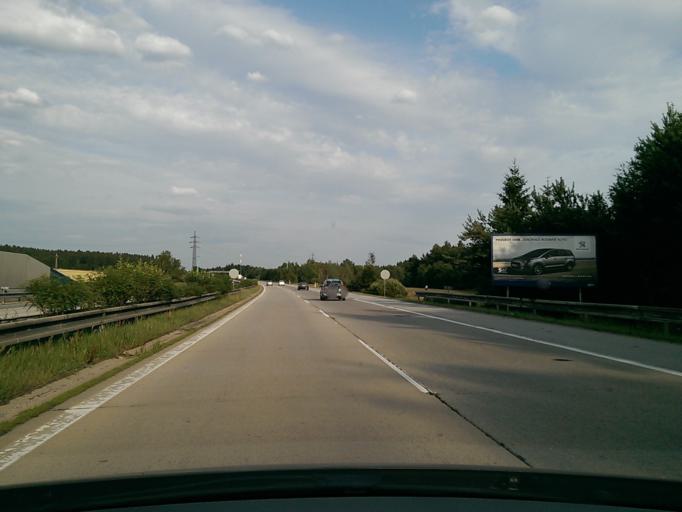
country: CZ
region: Vysocina
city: Velky Beranov
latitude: 49.4290
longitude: 15.6581
